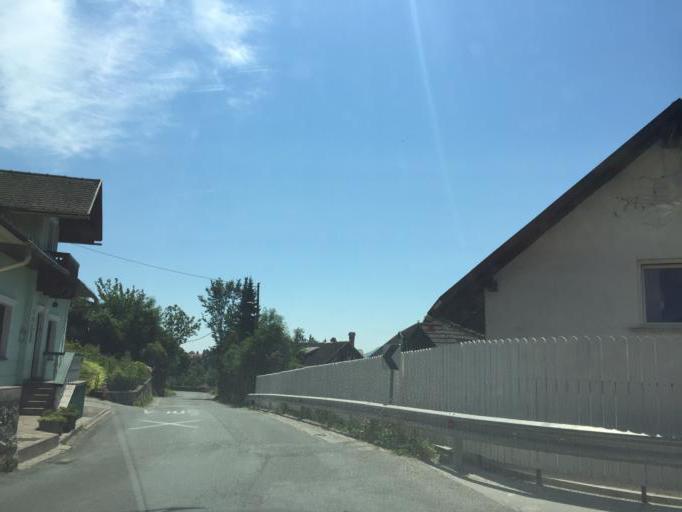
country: SI
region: Bled
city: Bled
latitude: 46.3726
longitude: 14.1044
